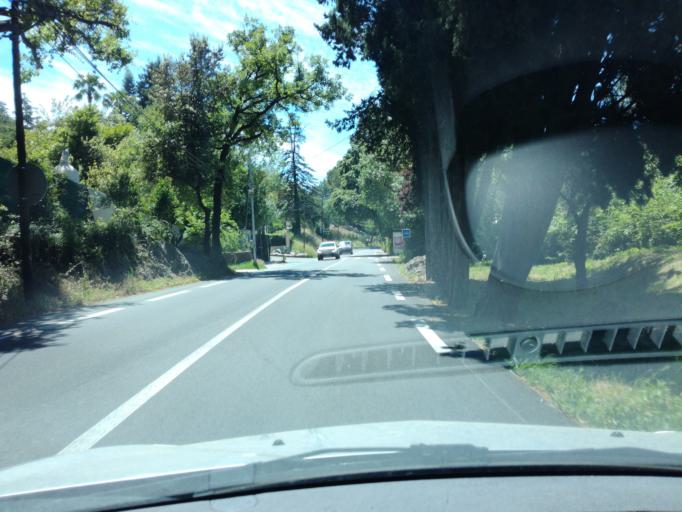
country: FR
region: Provence-Alpes-Cote d'Azur
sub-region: Departement des Alpes-Maritimes
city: Mougins
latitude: 43.5978
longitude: 7.0023
